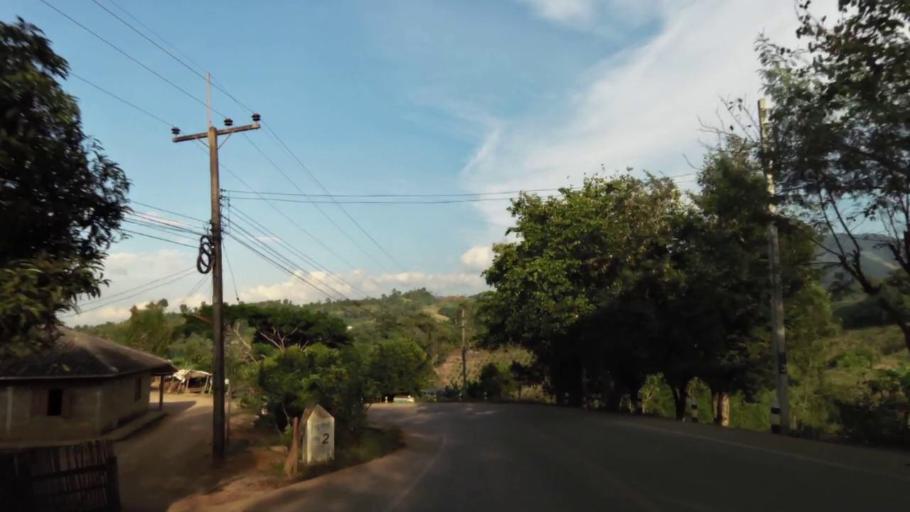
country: TH
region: Chiang Rai
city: Khun Tan
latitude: 19.8622
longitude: 100.3977
